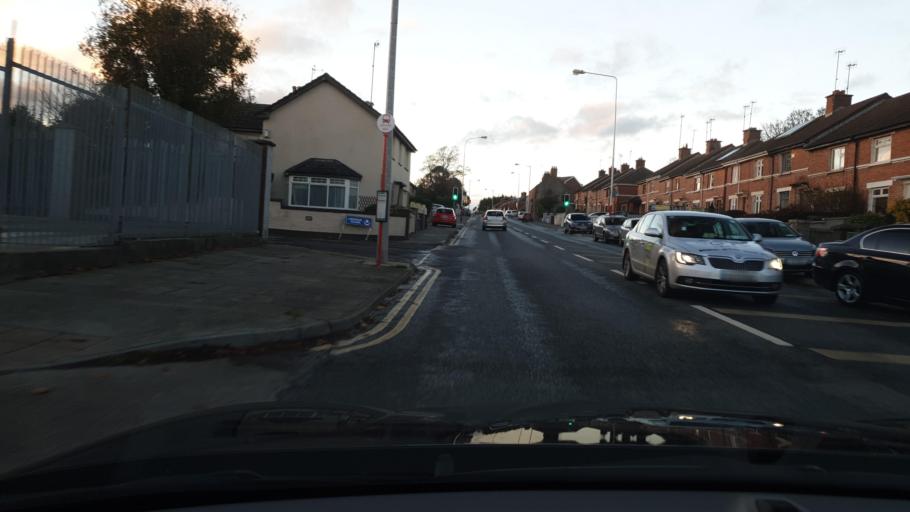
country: IE
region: Leinster
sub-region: Lu
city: Drogheda
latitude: 53.7200
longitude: -6.3570
